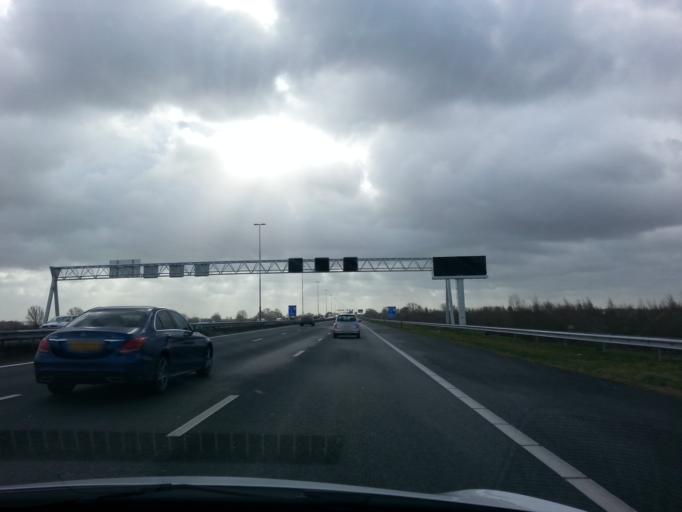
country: NL
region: Gelderland
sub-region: Gemeente Maasdriel
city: Hedel
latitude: 51.7469
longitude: 5.2957
